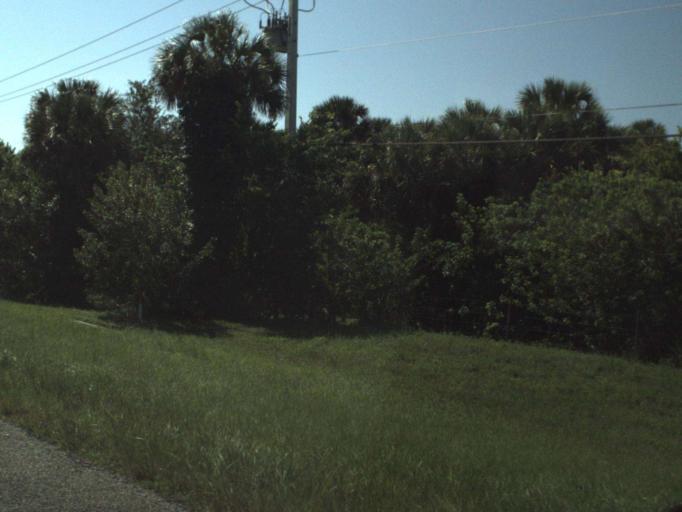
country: US
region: Florida
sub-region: Brevard County
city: Cocoa West
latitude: 28.3607
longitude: -80.8291
